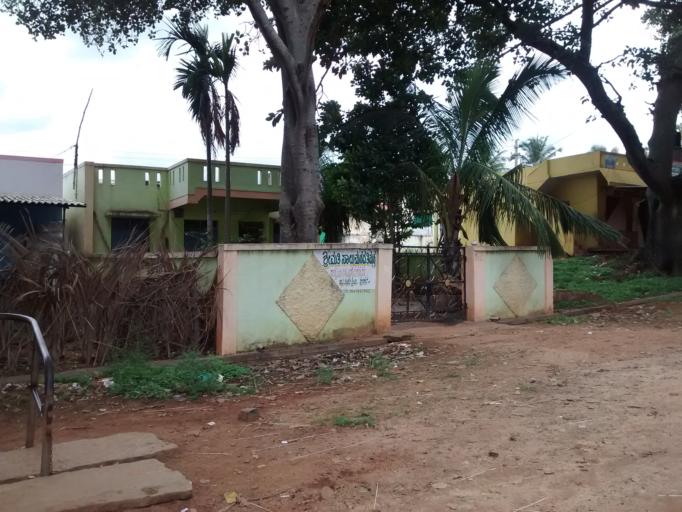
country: IN
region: Karnataka
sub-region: Tumkur
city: Kunigal
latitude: 13.1388
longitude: 77.1494
